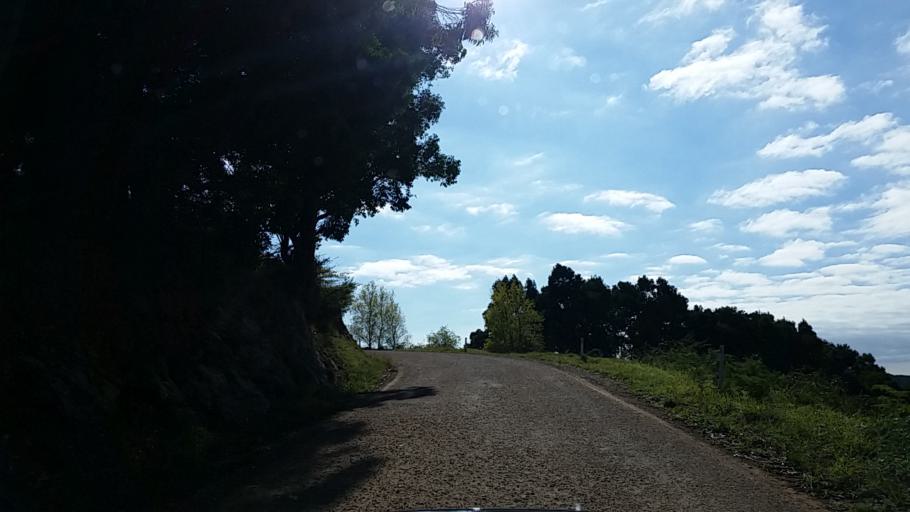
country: AU
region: South Australia
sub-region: Adelaide Hills
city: Adelaide Hills
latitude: -34.9526
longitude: 138.7175
